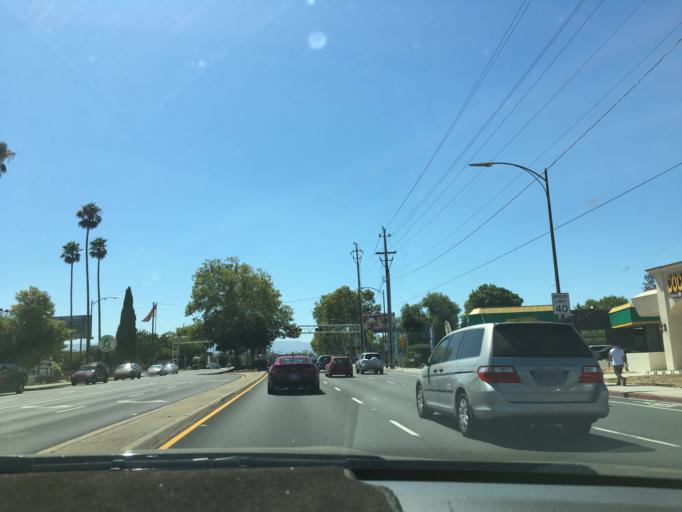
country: US
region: California
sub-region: Santa Clara County
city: Seven Trees
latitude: 37.2505
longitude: -121.8665
